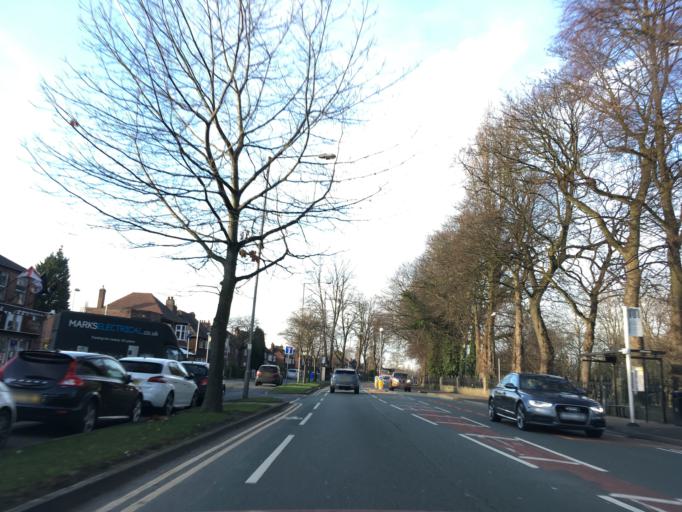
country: GB
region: England
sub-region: Manchester
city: Chorlton cum Hardy
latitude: 53.4283
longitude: -2.2629
